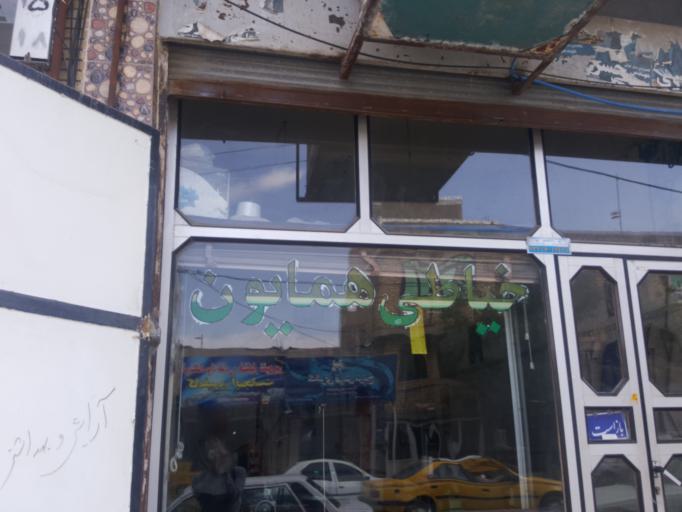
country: IR
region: Fars
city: Marvdasht
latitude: 29.8845
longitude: 52.8139
